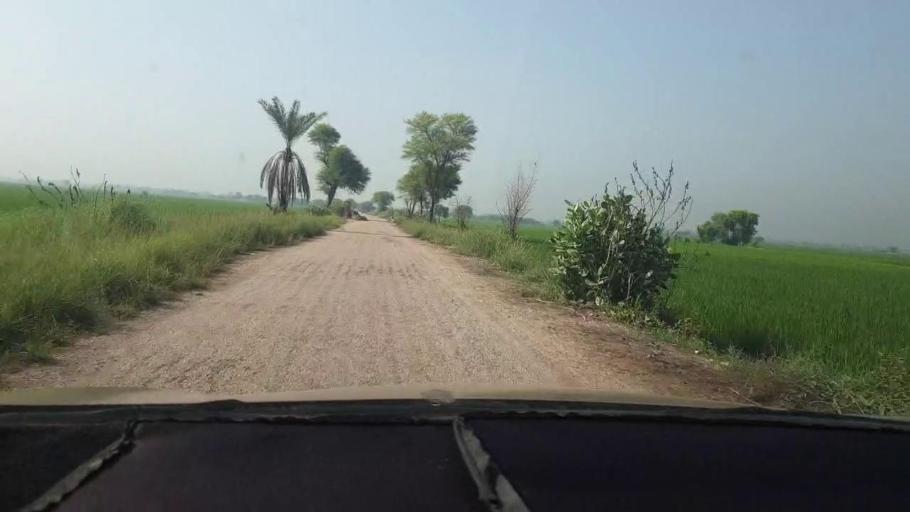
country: PK
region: Sindh
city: Kambar
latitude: 27.6302
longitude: 68.0897
